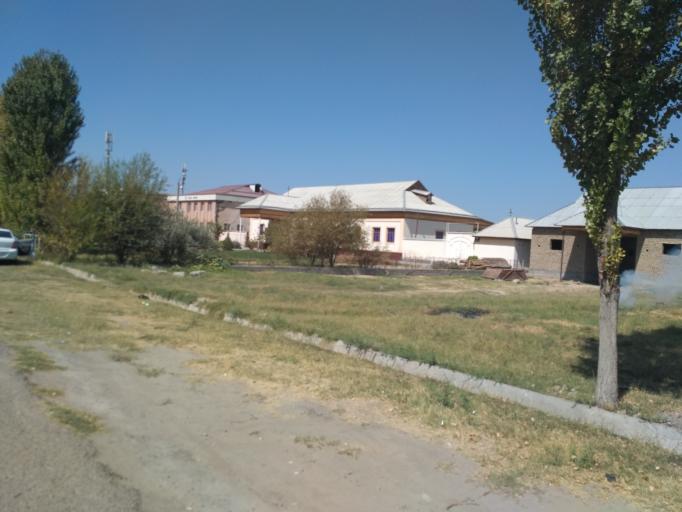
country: UZ
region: Sirdaryo
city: Guliston
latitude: 40.4957
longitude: 68.7056
